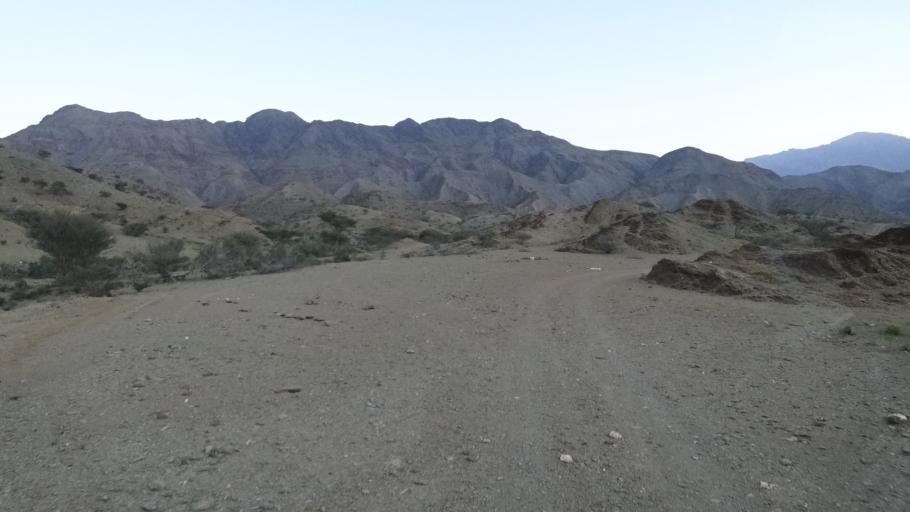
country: OM
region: Al Batinah
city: Rustaq
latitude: 23.2730
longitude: 57.3611
